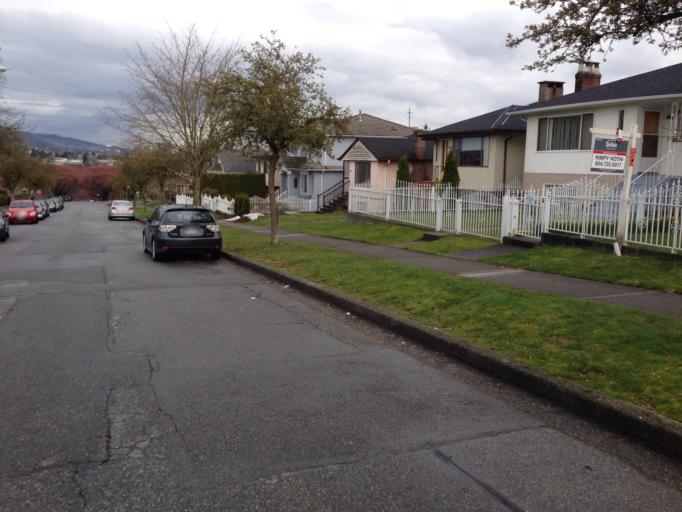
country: CA
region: British Columbia
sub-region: Fraser Valley Regional District
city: North Vancouver
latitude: 49.2704
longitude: -123.0407
